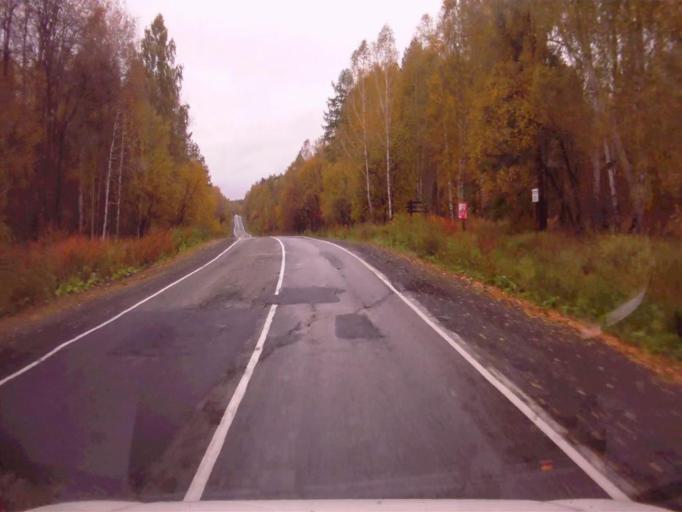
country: RU
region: Chelyabinsk
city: Nizhniy Ufaley
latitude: 56.0518
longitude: 59.9500
